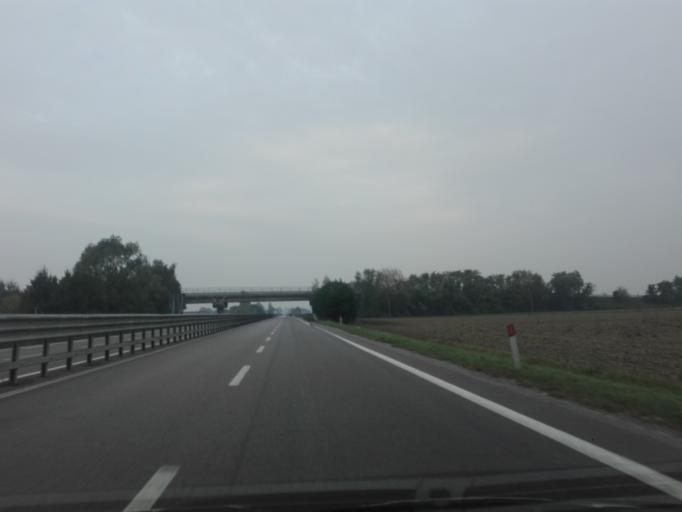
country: IT
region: Veneto
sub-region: Provincia di Rovigo
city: Villamarzana
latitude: 45.0214
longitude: 11.6768
